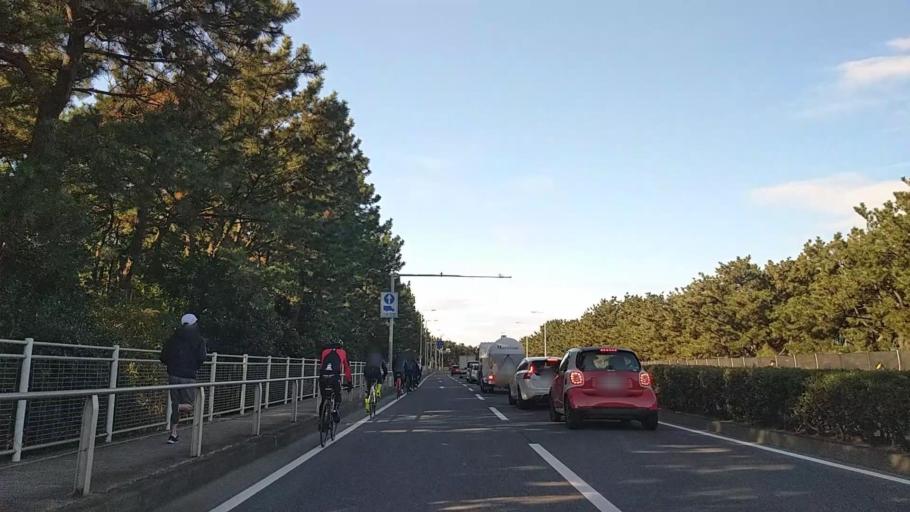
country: JP
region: Kanagawa
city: Chigasaki
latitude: 35.3186
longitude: 139.4207
